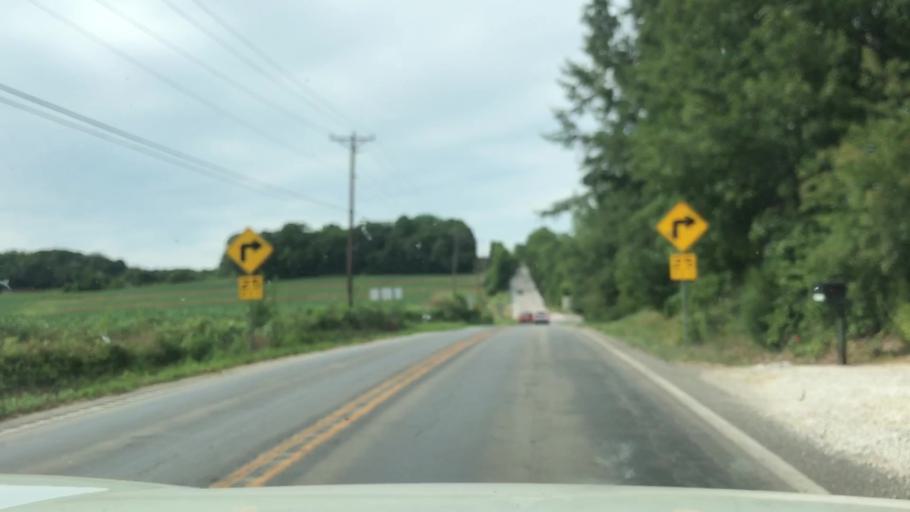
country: US
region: Missouri
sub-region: Saint Charles County
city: Weldon Spring
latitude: 38.6513
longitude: -90.7761
